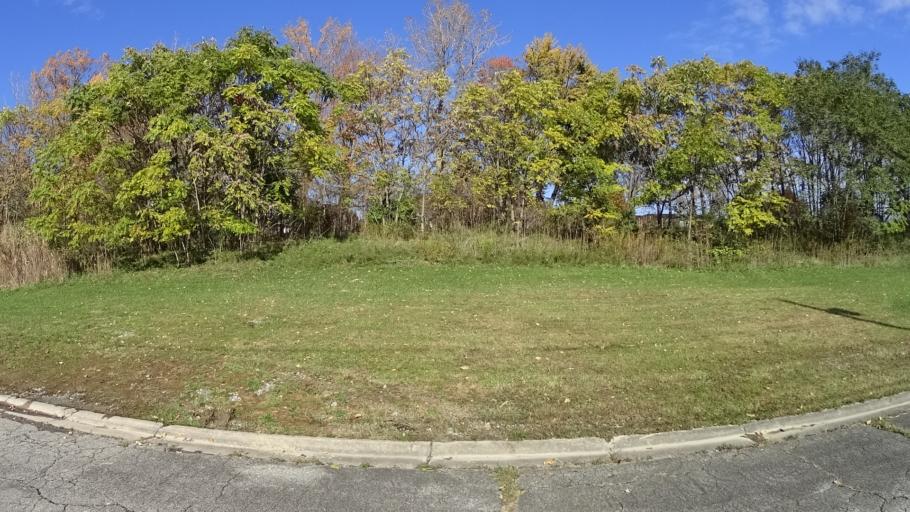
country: US
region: Ohio
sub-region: Lorain County
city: Lorain
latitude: 41.4460
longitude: -82.2177
